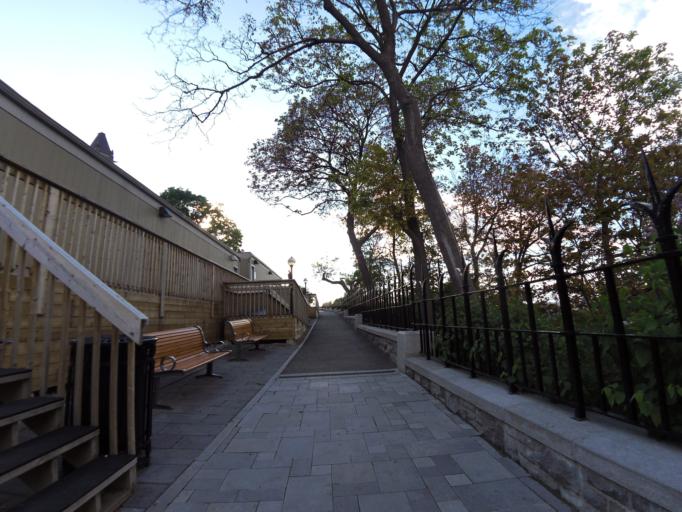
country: CA
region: Ontario
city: Ottawa
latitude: 45.4255
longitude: -75.6981
